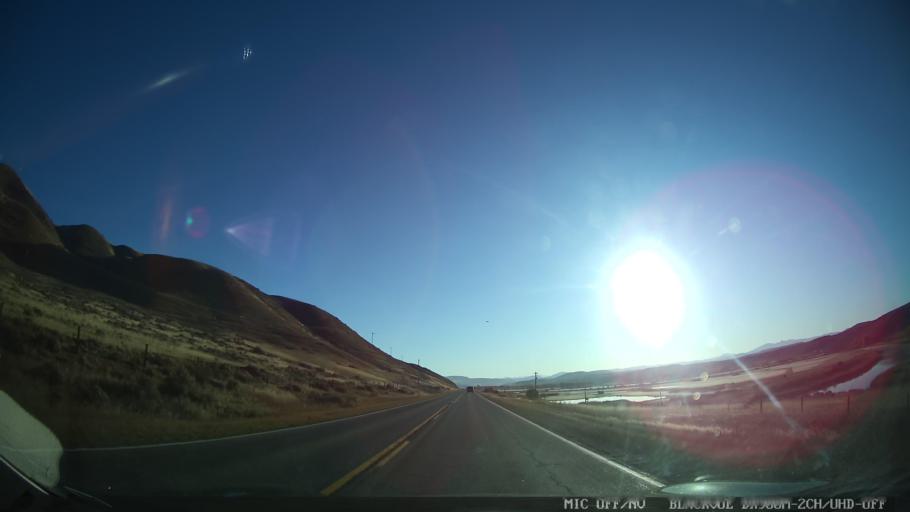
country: US
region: Colorado
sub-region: Grand County
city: Kremmling
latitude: 40.0516
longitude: -106.3444
